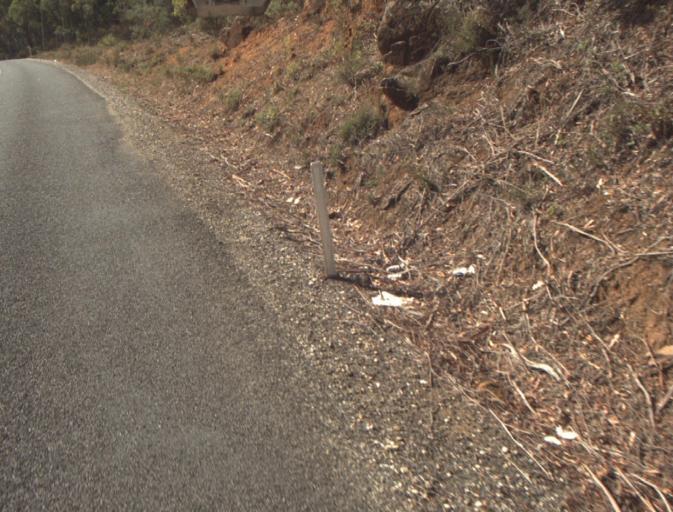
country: AU
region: Tasmania
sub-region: Launceston
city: Mayfield
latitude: -41.3011
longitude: 147.1334
